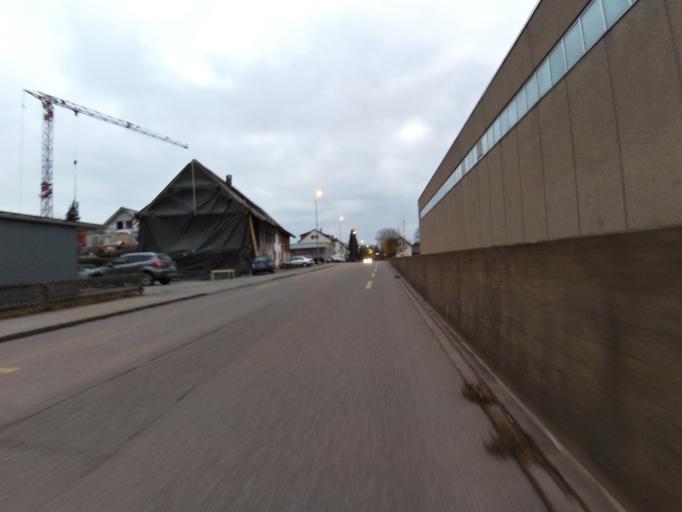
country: CH
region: Thurgau
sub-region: Frauenfeld District
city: Frauenfeld
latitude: 47.5644
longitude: 8.9021
